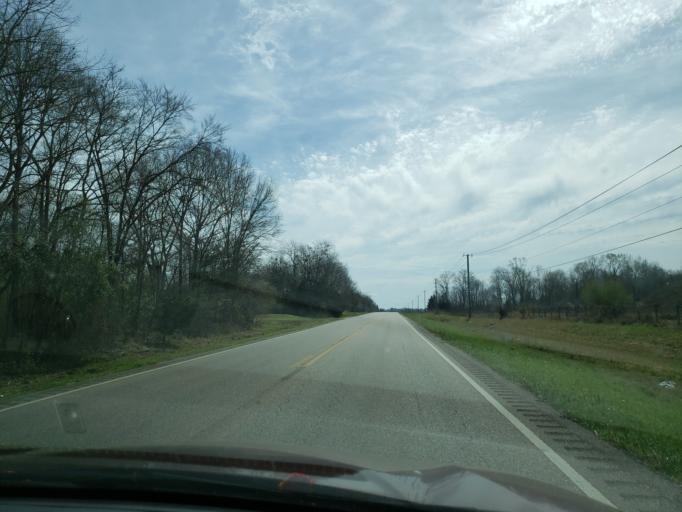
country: US
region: Alabama
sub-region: Dallas County
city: Selma
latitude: 32.4455
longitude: -87.0724
